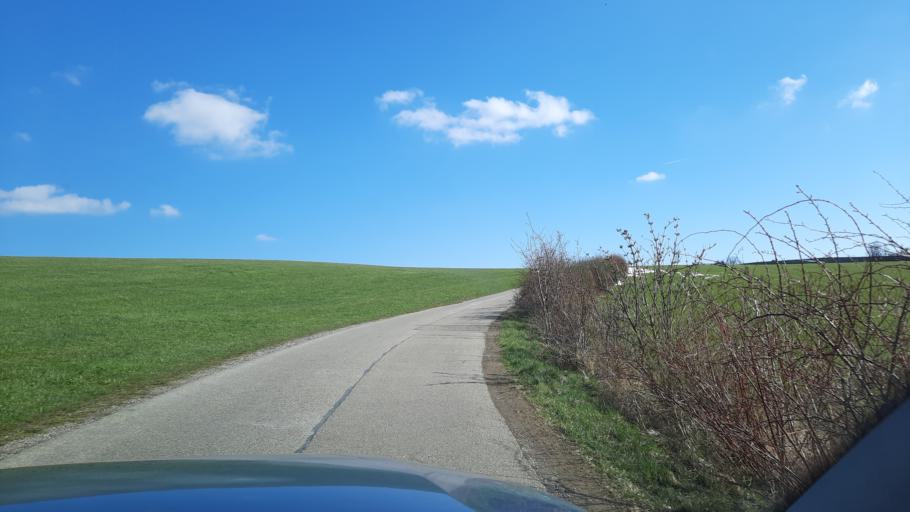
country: DE
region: Bavaria
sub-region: Swabia
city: Altusried
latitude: 47.8191
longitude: 10.1982
